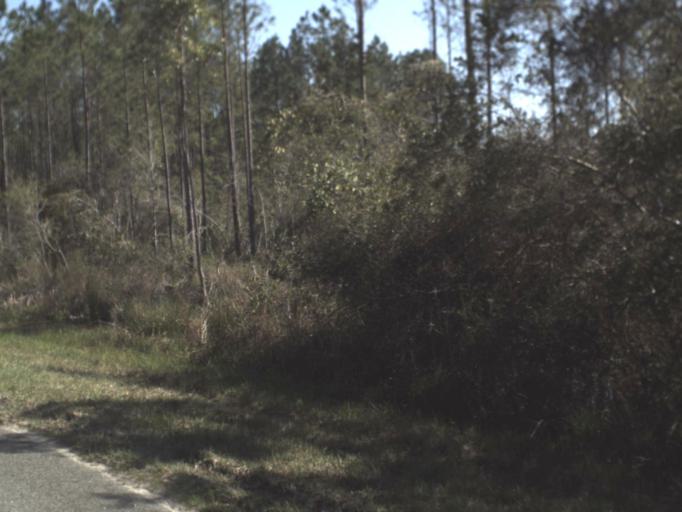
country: US
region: Florida
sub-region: Leon County
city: Woodville
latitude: 30.3095
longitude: -84.0472
